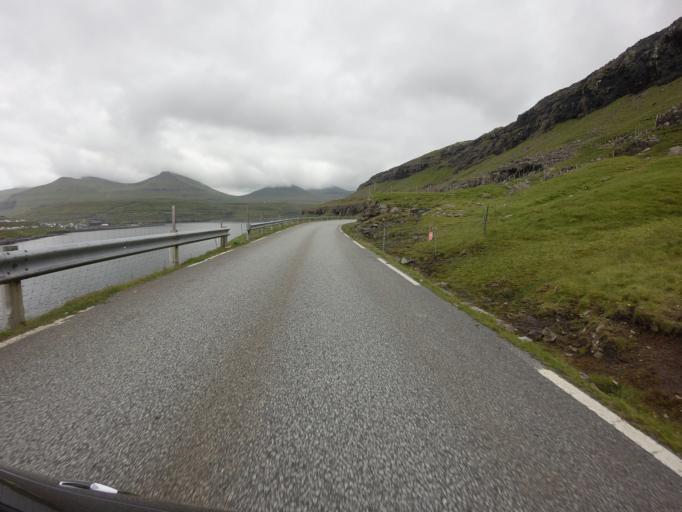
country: FO
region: Eysturoy
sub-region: Eidi
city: Eidi
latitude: 62.2938
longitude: -7.1232
